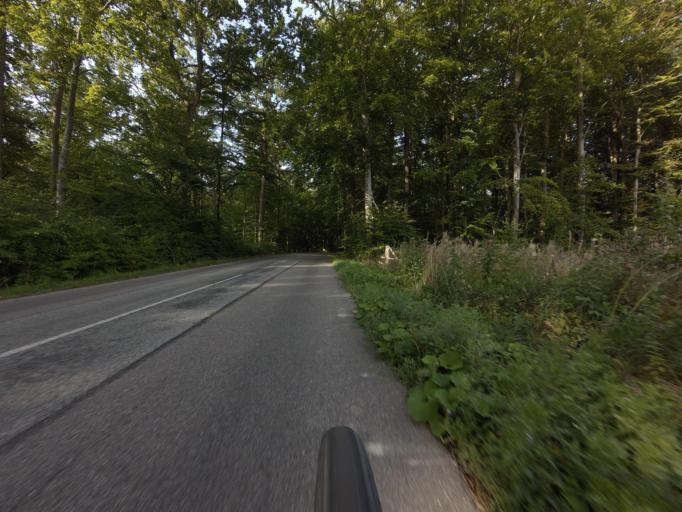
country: DK
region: Zealand
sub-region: Faxe Kommune
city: Fakse Ladeplads
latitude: 55.2322
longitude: 12.2016
